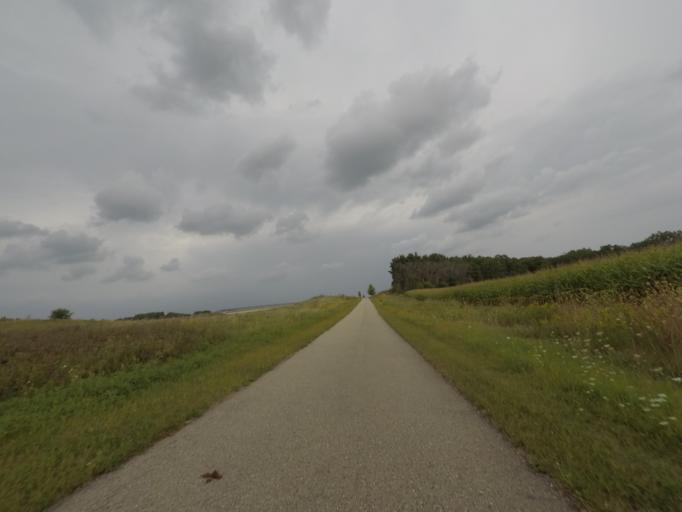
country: US
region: Wisconsin
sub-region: Jefferson County
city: Jefferson
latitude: 42.9831
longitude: -88.8274
